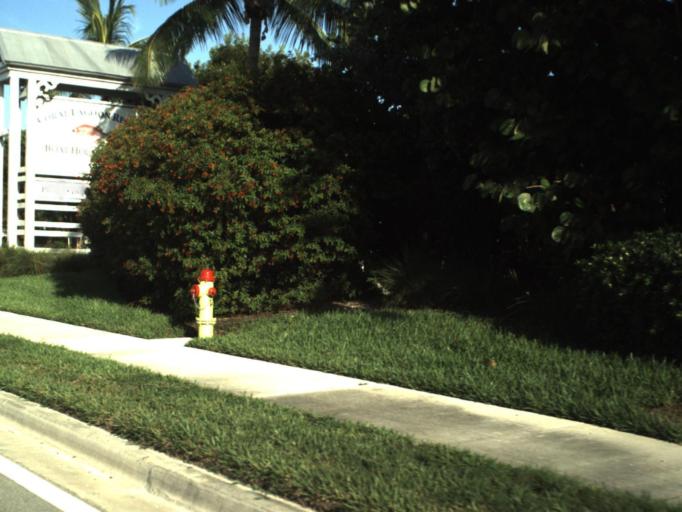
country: US
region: Florida
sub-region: Monroe County
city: Marathon
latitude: 24.7311
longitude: -81.0254
